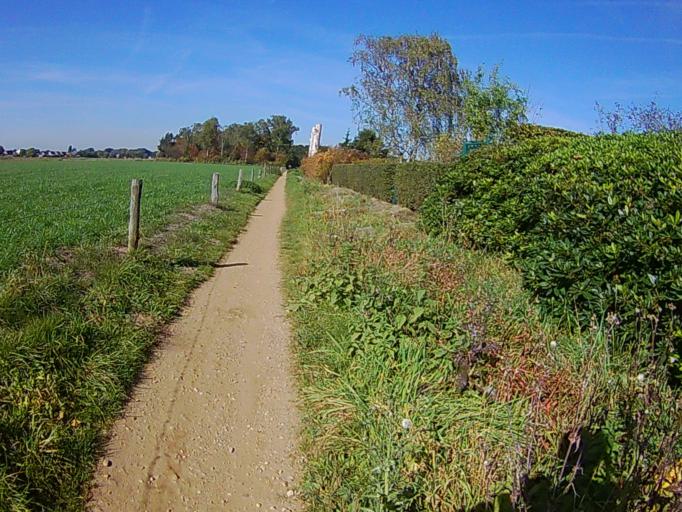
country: BE
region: Flanders
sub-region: Provincie Antwerpen
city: Stabroek
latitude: 51.3315
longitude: 4.3910
